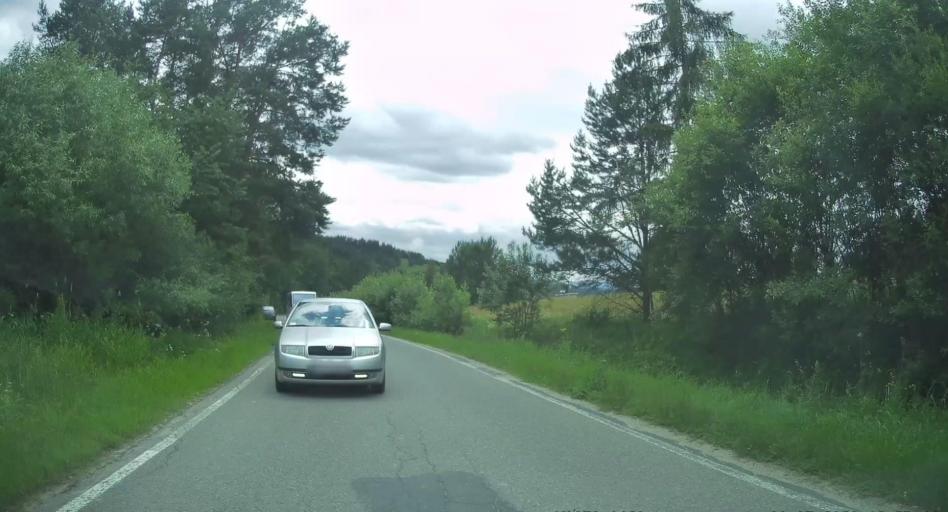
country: PL
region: Lesser Poland Voivodeship
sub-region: Powiat nowosadecki
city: Muszyna
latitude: 49.3883
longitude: 20.9025
